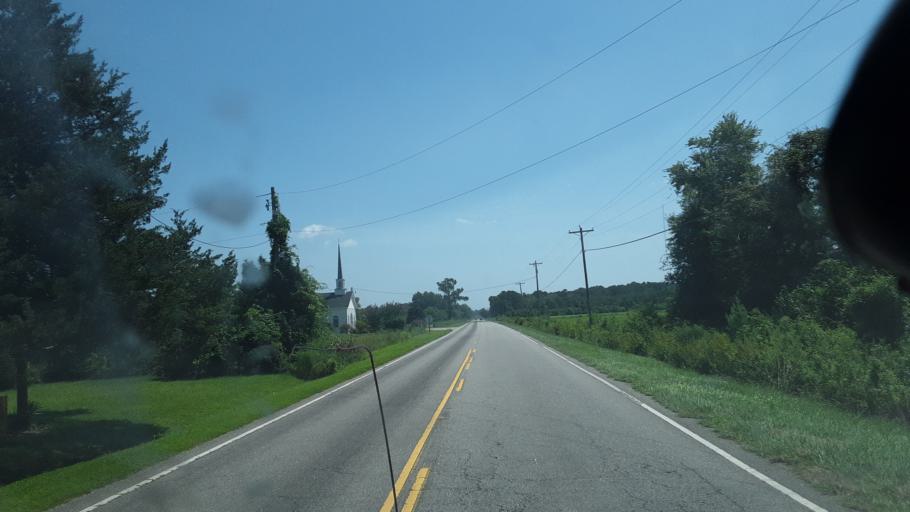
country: US
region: South Carolina
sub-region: Horry County
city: North Myrtle Beach
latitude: 33.8600
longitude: -78.7243
